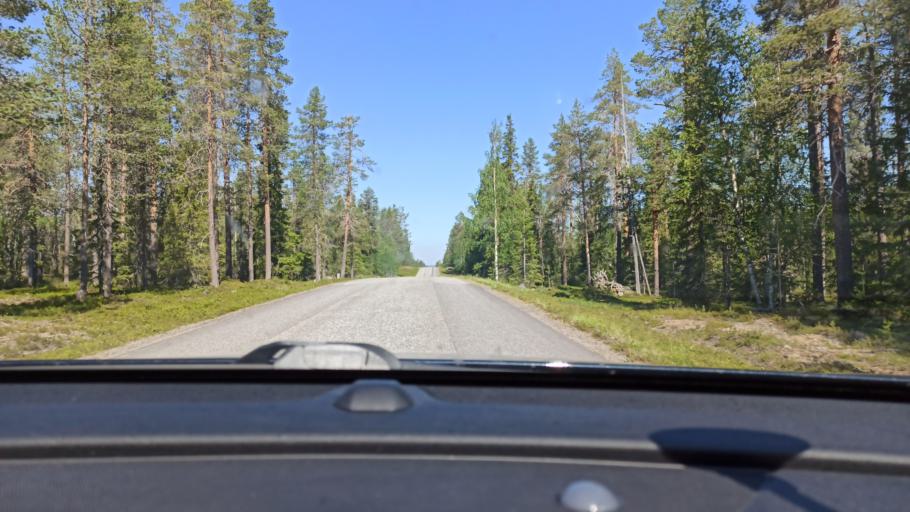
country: FI
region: Lapland
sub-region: Tunturi-Lappi
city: Kolari
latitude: 67.6734
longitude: 24.1467
